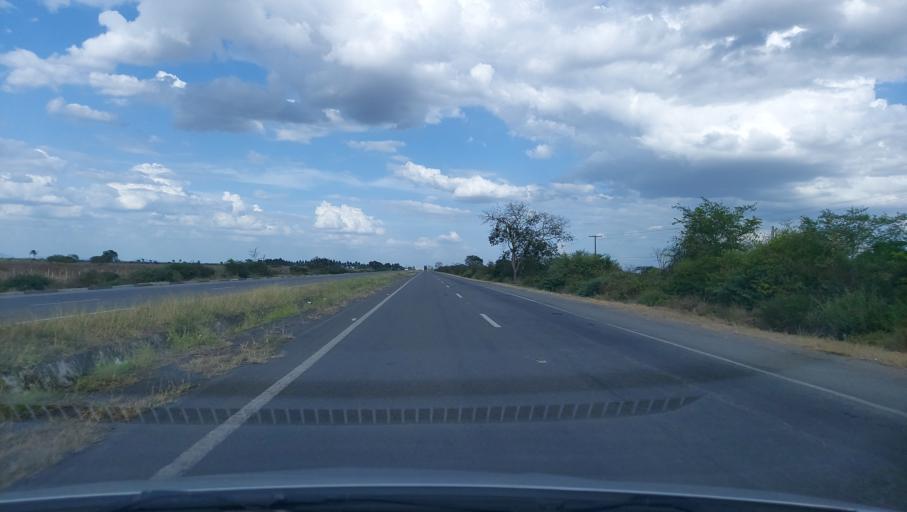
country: BR
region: Bahia
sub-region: Castro Alves
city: Castro Alves
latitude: -12.5551
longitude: -39.4619
